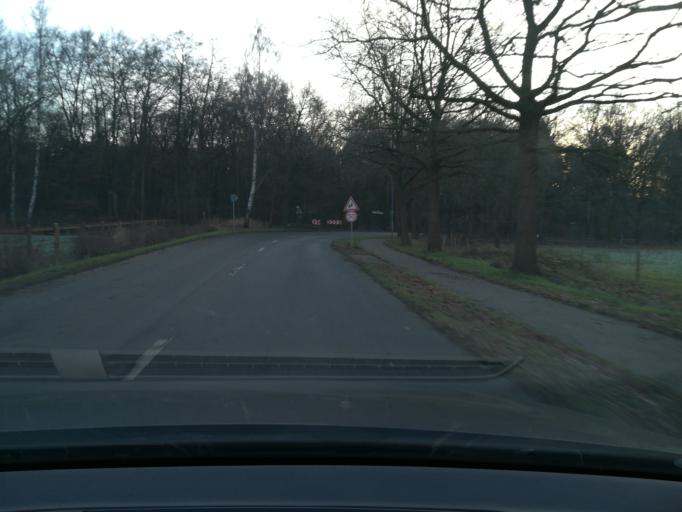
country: DE
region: Schleswig-Holstein
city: Escheburg
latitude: 53.4528
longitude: 10.3144
